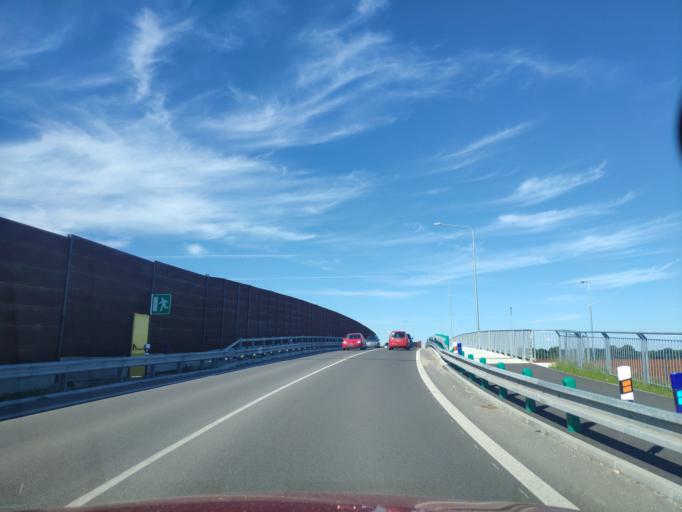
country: SK
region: Bratislavsky
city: Svaty Jur
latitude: 48.2109
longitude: 17.2216
